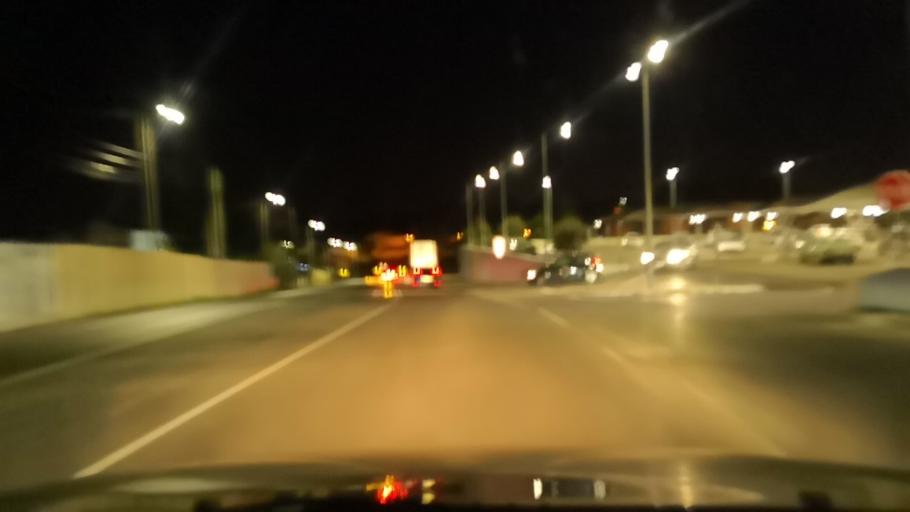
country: PT
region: Setubal
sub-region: Palmela
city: Palmela
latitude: 38.5778
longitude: -8.8981
